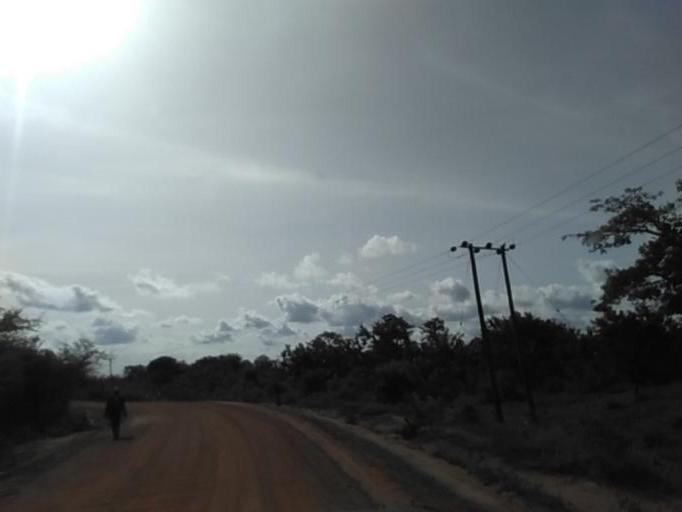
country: GH
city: Akropong
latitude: 6.0844
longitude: 0.2750
